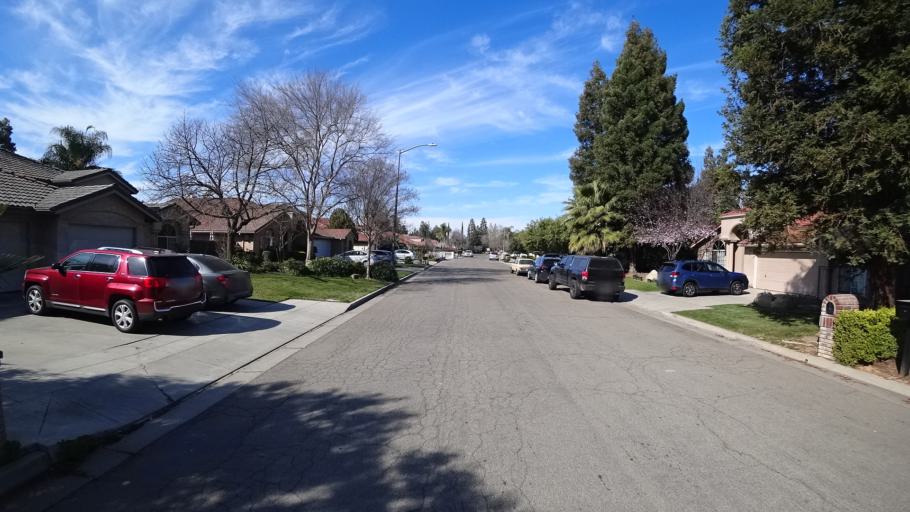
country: US
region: California
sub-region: Fresno County
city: Clovis
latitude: 36.8579
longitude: -119.7492
